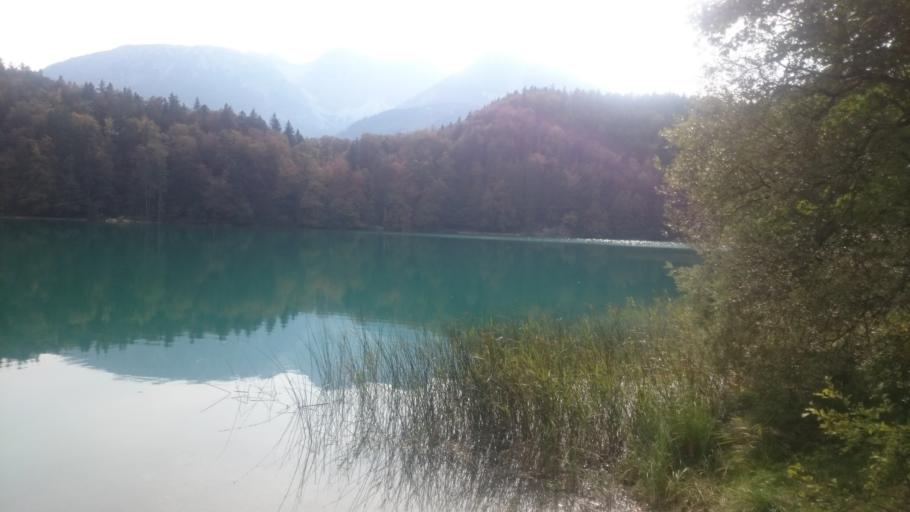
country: AT
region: Tyrol
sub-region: Politischer Bezirk Reutte
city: Vils
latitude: 47.5627
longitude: 10.6389
